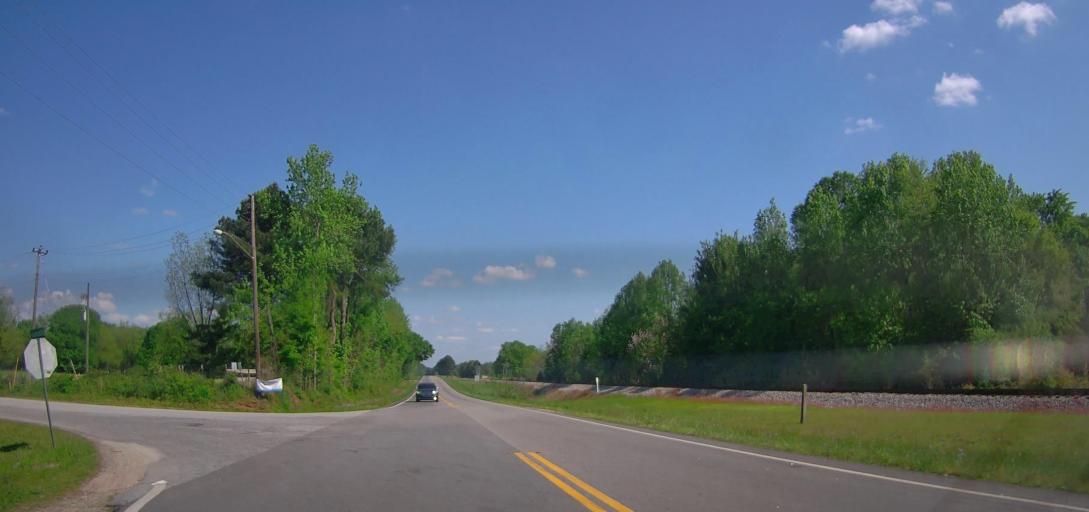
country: US
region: Georgia
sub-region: Morgan County
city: Madison
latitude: 33.6096
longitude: -83.4338
